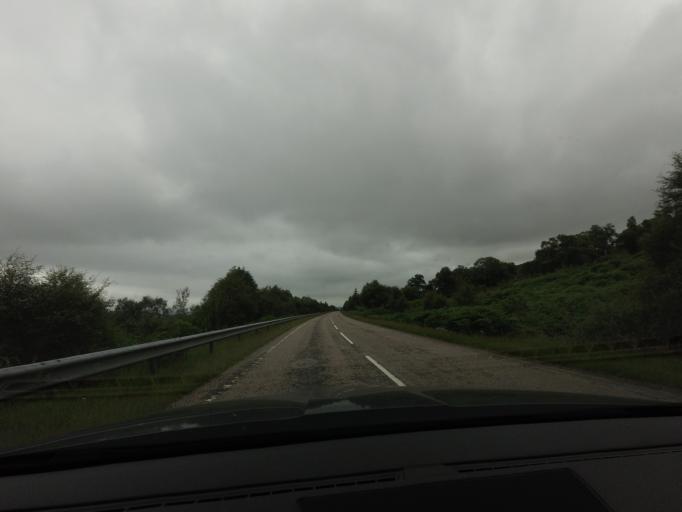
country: GB
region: Scotland
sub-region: Highland
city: Alness
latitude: 57.9905
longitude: -4.4038
